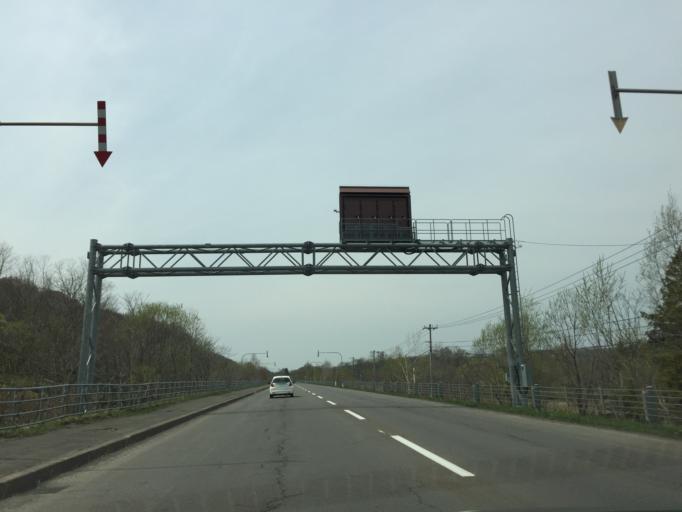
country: JP
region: Hokkaido
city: Ashibetsu
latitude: 43.5331
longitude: 142.1635
